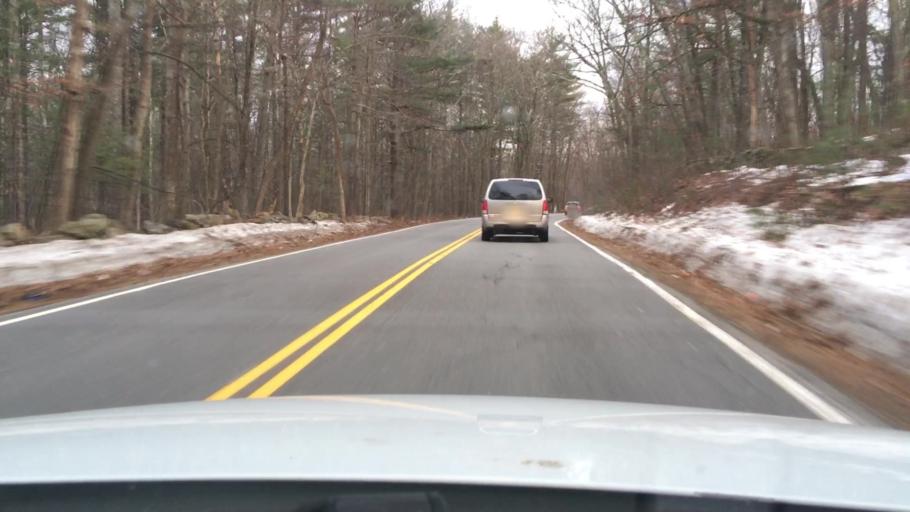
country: US
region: New Hampshire
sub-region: Rockingham County
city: Atkinson
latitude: 42.8320
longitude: -71.1409
